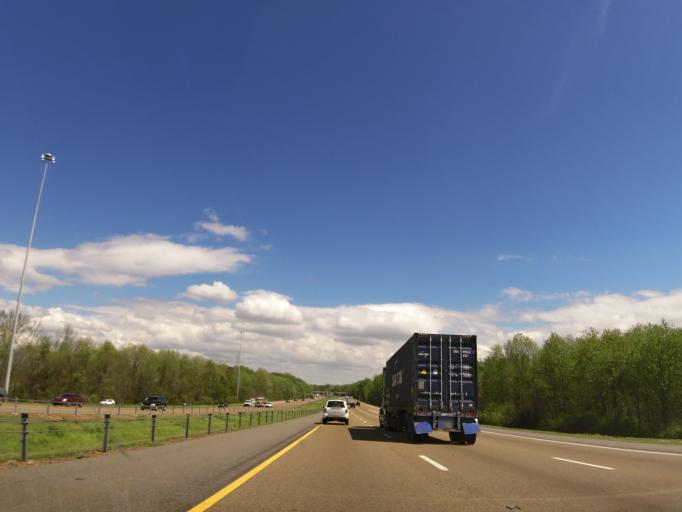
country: US
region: Tennessee
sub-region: Shelby County
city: Bartlett
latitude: 35.1903
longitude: -89.9544
